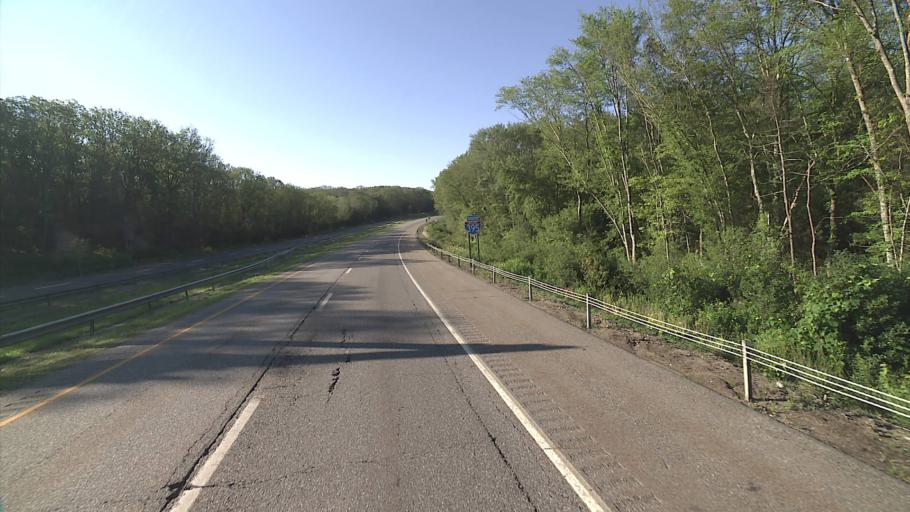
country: US
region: Connecticut
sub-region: Windham County
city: Danielson
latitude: 41.7872
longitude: -71.8734
